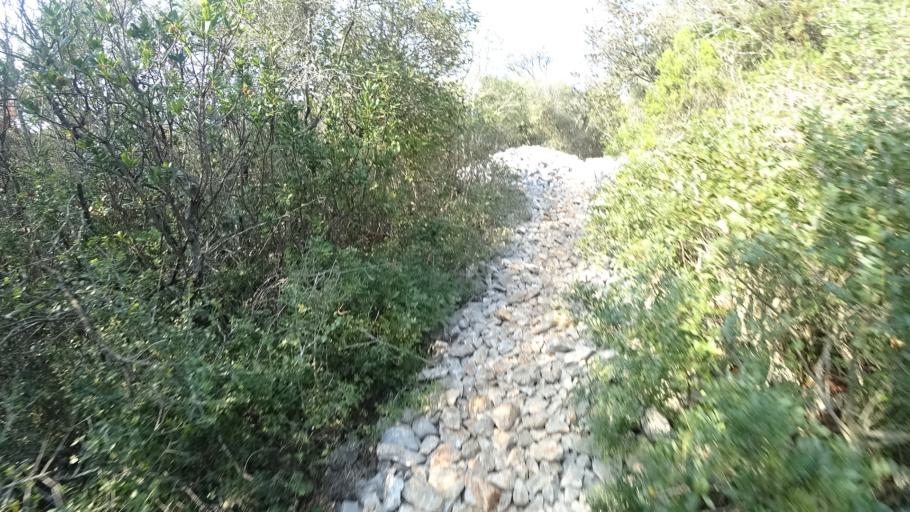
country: HR
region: Primorsko-Goranska
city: Mali Losinj
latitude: 44.4898
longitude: 14.5056
